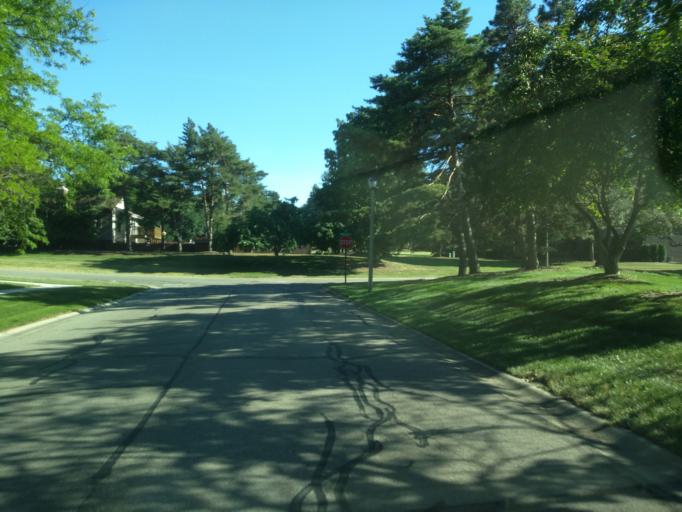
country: US
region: Michigan
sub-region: Eaton County
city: Waverly
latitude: 42.7257
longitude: -84.6351
